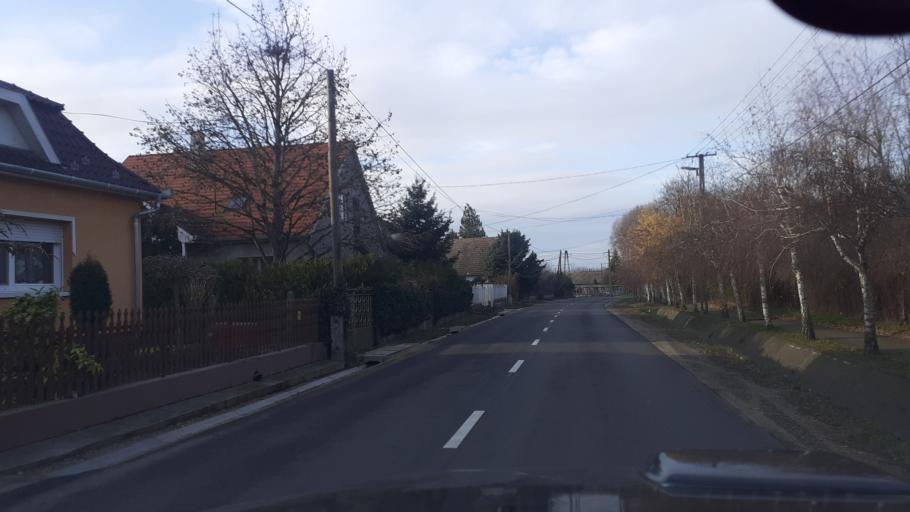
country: HU
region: Bacs-Kiskun
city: Tass
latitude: 47.0237
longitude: 19.0268
